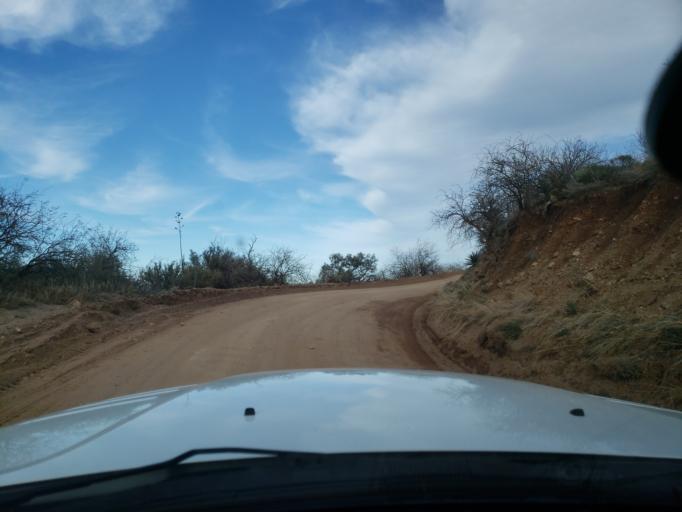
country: US
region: Arizona
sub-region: Pinal County
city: Oracle
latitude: 32.5484
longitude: -110.7079
